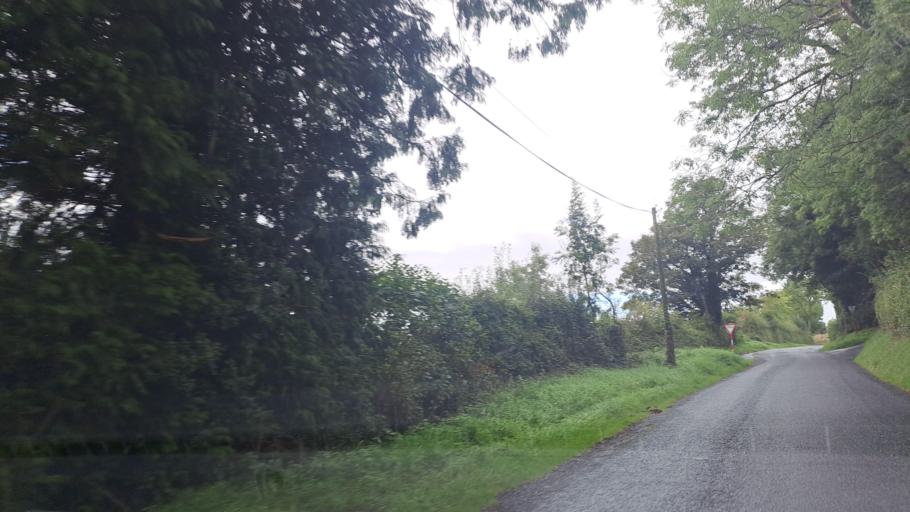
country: IE
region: Ulster
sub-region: County Monaghan
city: Carrickmacross
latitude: 53.9717
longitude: -6.7538
